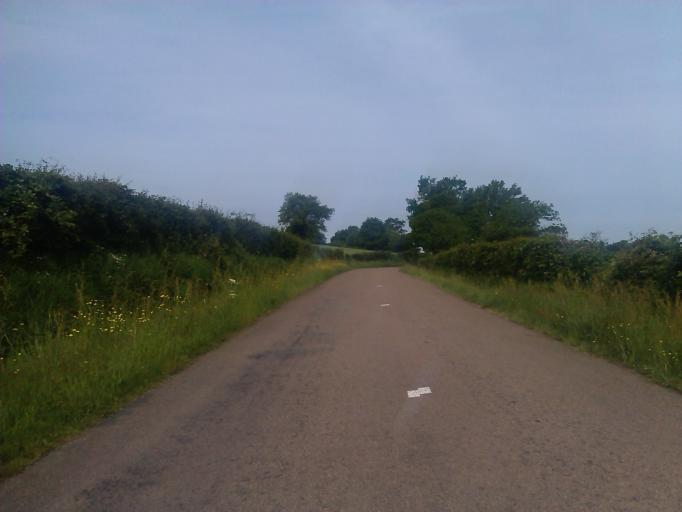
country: FR
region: Auvergne
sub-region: Departement de l'Allier
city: Cerilly
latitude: 46.6166
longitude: 2.7582
